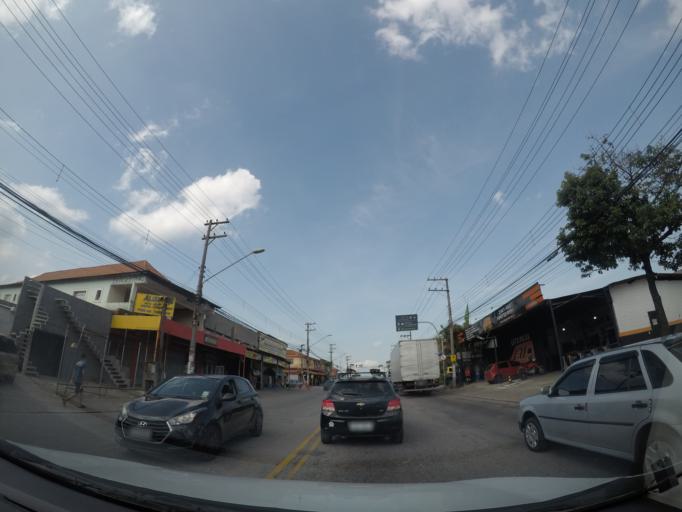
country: BR
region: Sao Paulo
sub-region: Guarulhos
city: Guarulhos
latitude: -23.4325
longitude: -46.4403
